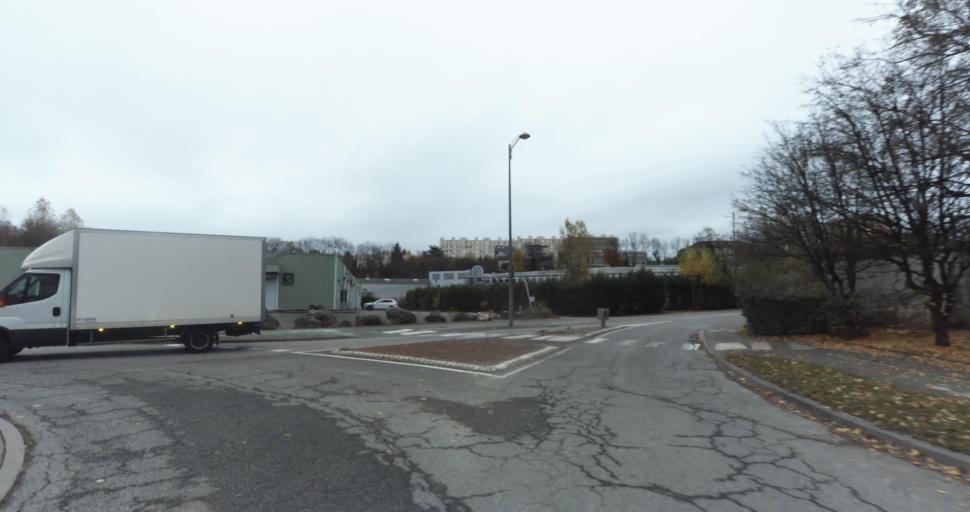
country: FR
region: Rhone-Alpes
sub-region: Departement de la Haute-Savoie
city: Cran-Gevrier
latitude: 45.9126
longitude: 6.1080
